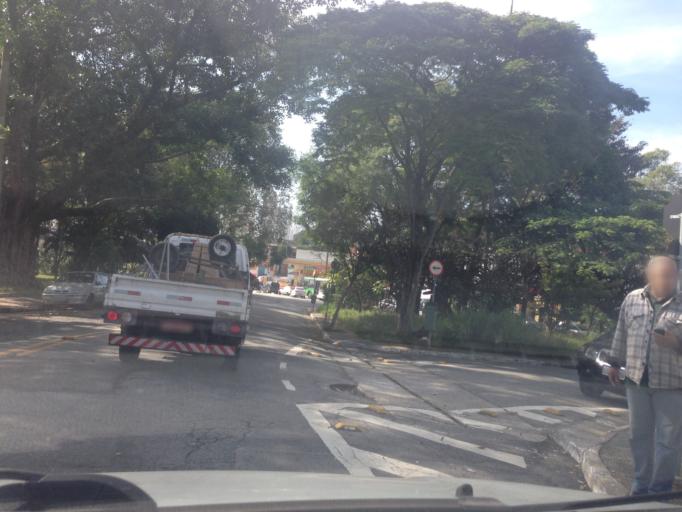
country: BR
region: Sao Paulo
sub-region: Sao Paulo
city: Sao Paulo
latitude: -23.5281
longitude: -46.7060
